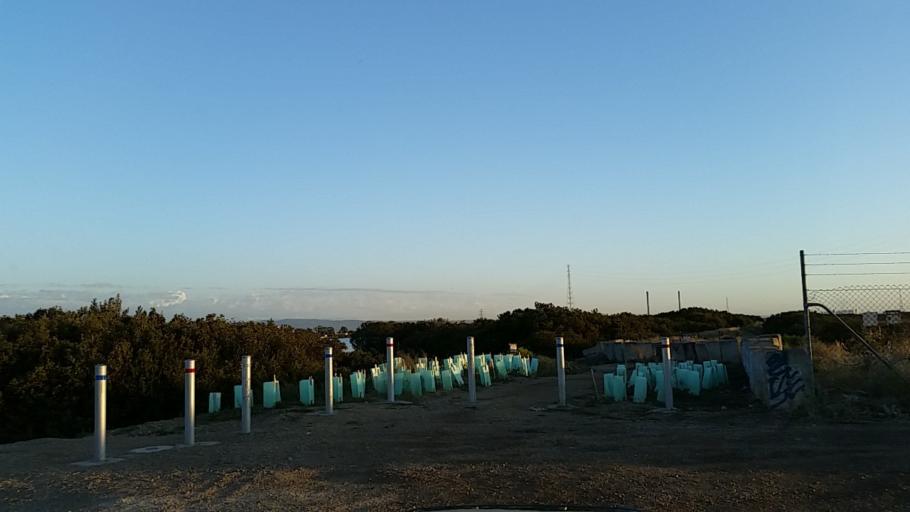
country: AU
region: South Australia
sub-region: Port Adelaide Enfield
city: Birkenhead
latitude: -34.7710
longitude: 138.5144
